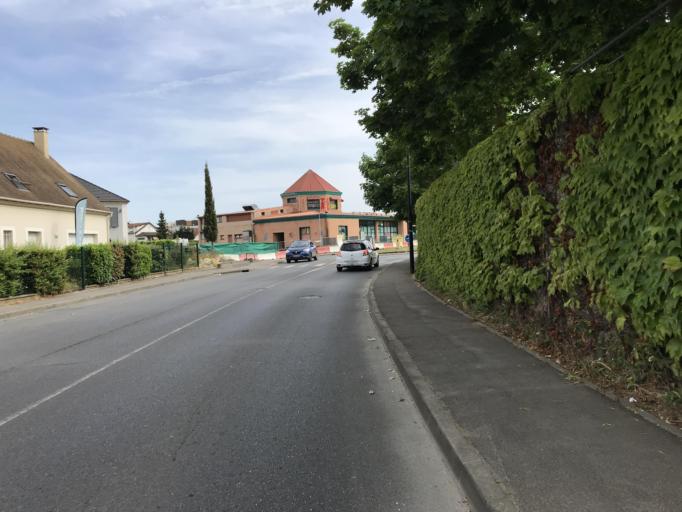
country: FR
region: Ile-de-France
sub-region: Departement de l'Essonne
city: La Ville-du-Bois
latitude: 48.6692
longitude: 2.2781
